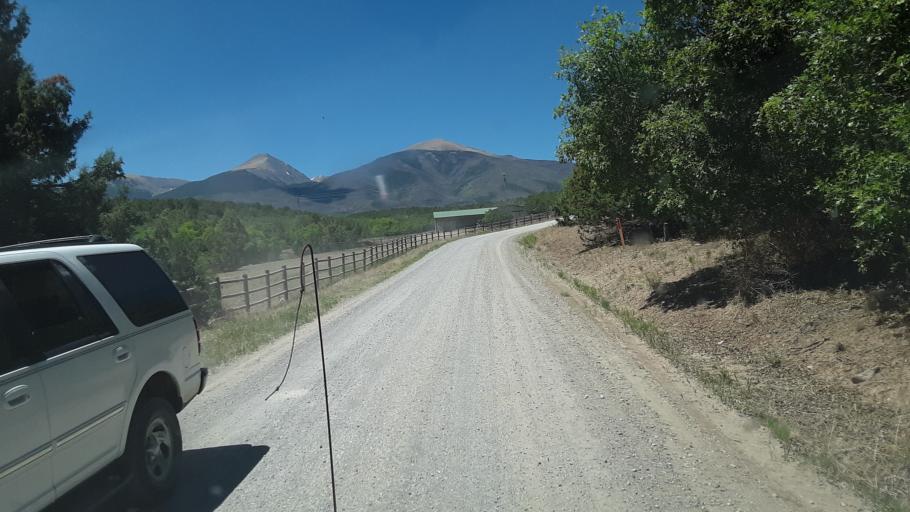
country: US
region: Colorado
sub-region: Custer County
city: Westcliffe
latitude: 38.3181
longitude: -105.6642
